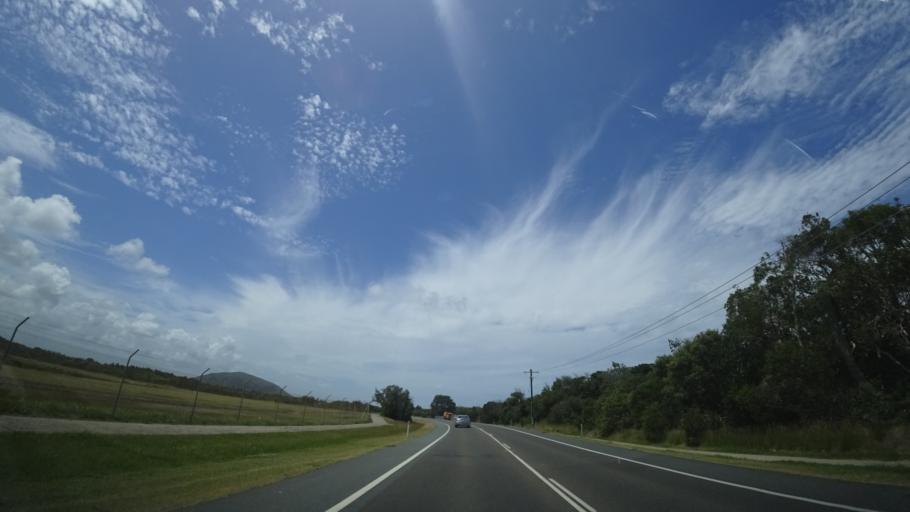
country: AU
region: Queensland
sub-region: Sunshine Coast
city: Coolum Beach
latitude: -26.5932
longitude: 153.0962
